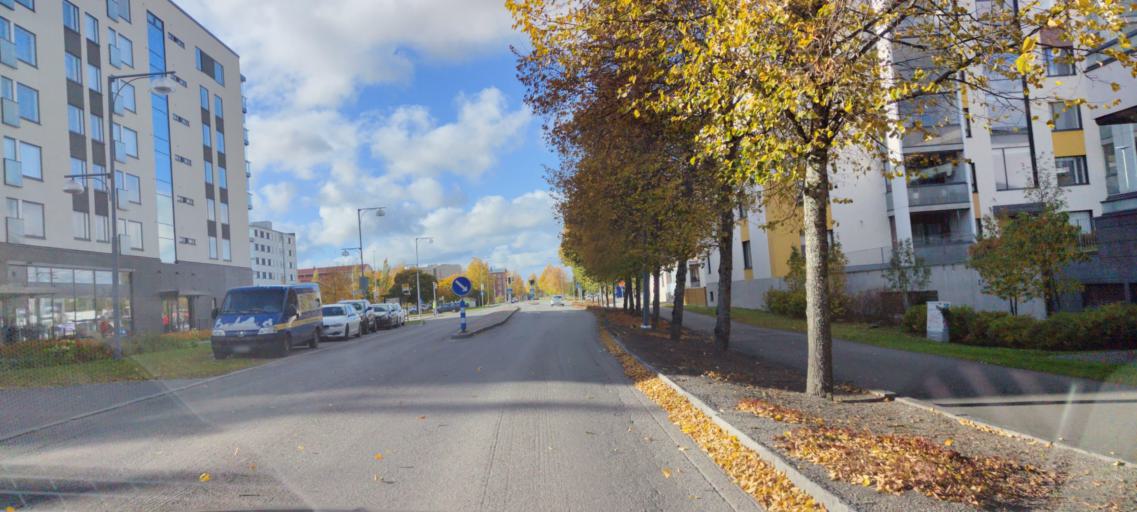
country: FI
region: Varsinais-Suomi
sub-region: Turku
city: Kaarina
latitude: 60.4071
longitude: 22.3651
